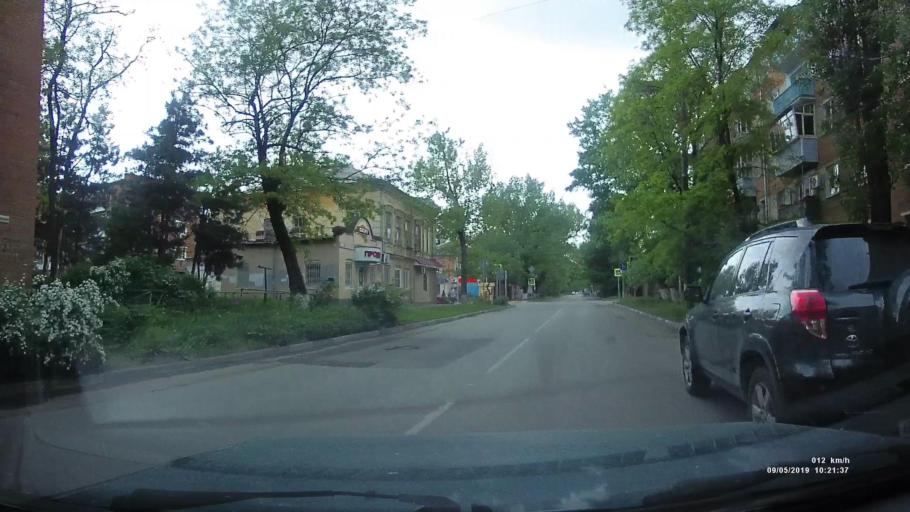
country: RU
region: Rostov
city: Azov
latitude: 47.1068
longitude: 39.4257
